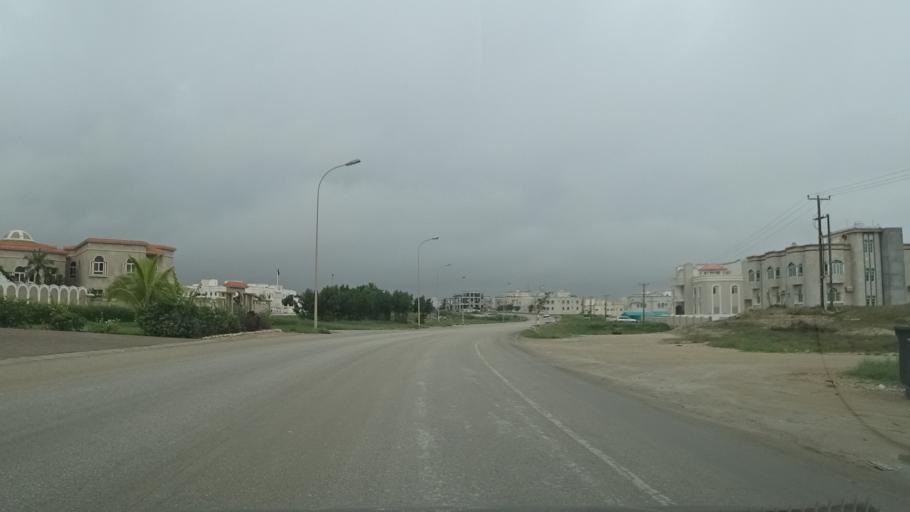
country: OM
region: Zufar
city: Salalah
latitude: 17.0055
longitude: 54.0323
